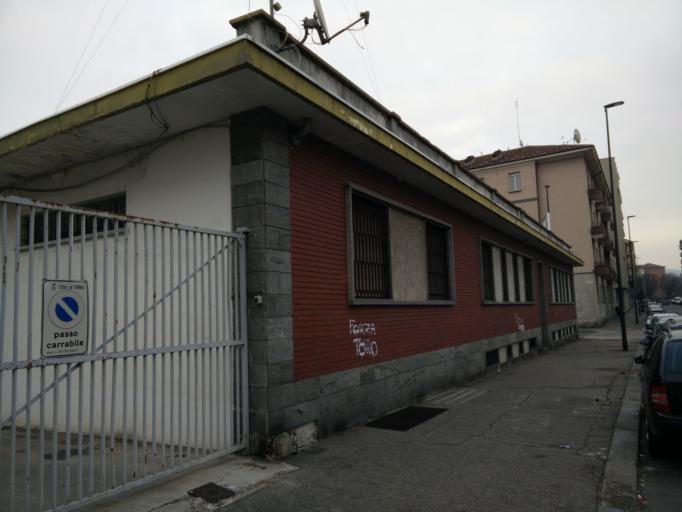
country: IT
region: Piedmont
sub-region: Provincia di Torino
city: Nichelino
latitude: 45.0191
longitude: 7.6533
